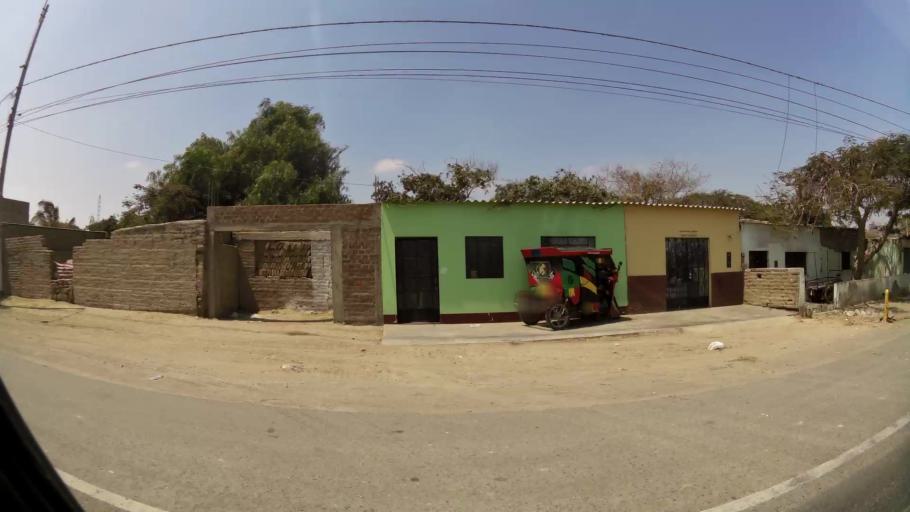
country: PE
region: La Libertad
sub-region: Provincia de Pacasmayo
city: Pacasmayo
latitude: -7.3970
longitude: -79.5578
